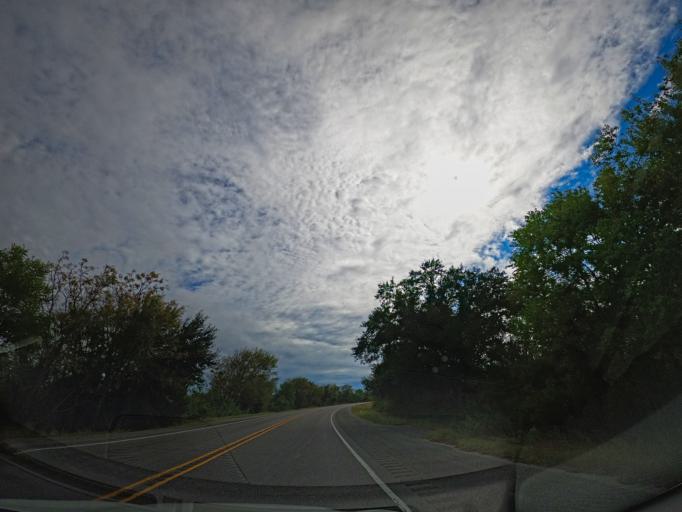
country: US
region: Louisiana
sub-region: Saint Tammany Parish
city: Eden Isle
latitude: 30.0801
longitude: -89.7918
